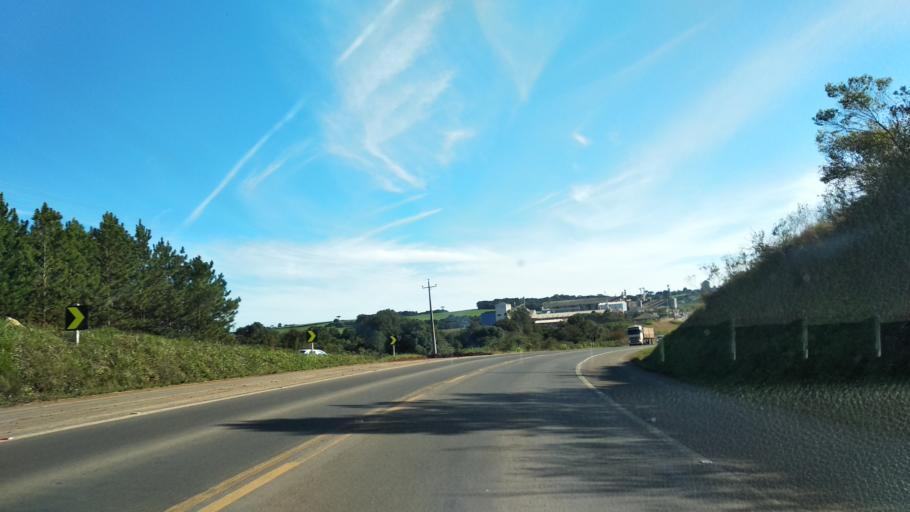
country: BR
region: Santa Catarina
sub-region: Campos Novos
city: Campos Novos
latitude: -27.4076
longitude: -51.2093
